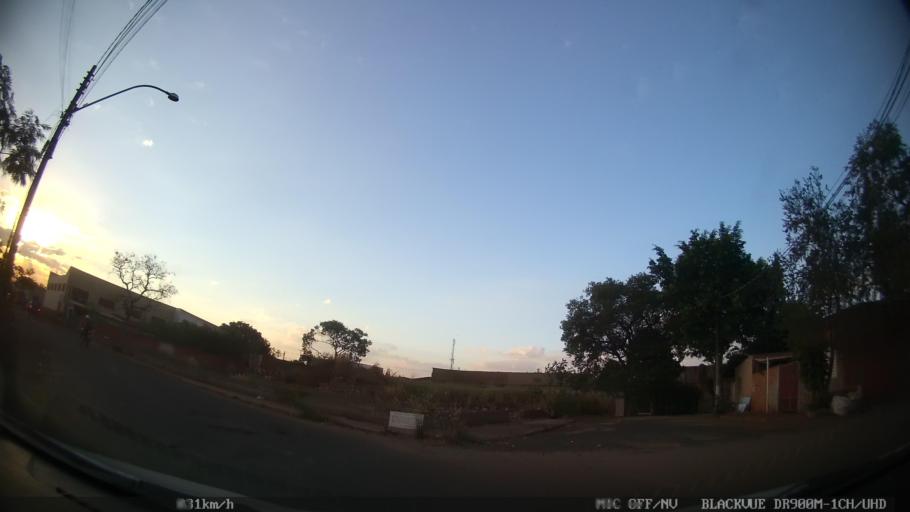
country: BR
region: Sao Paulo
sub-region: Ribeirao Preto
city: Ribeirao Preto
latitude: -21.1464
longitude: -47.7886
